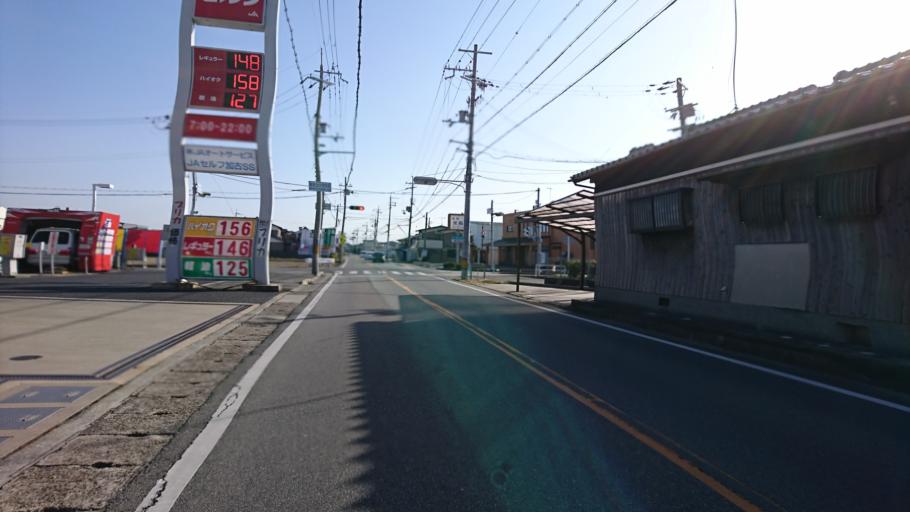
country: JP
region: Hyogo
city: Kakogawacho-honmachi
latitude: 34.7630
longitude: 134.9076
